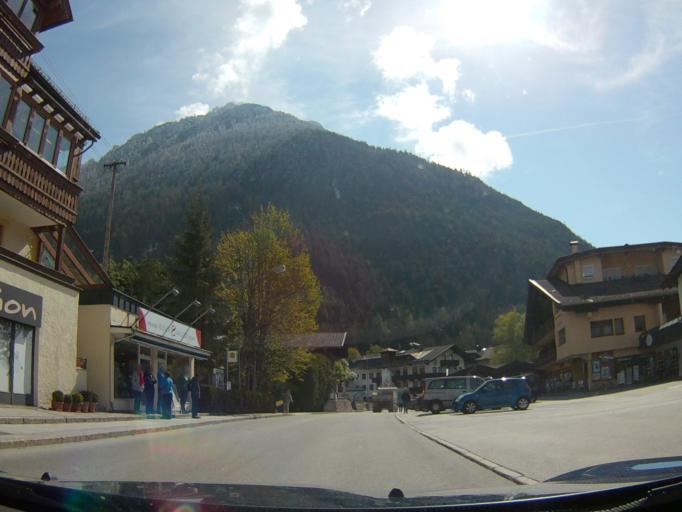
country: AT
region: Tyrol
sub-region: Politischer Bezirk Schwaz
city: Jenbach
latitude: 47.4225
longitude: 11.7519
